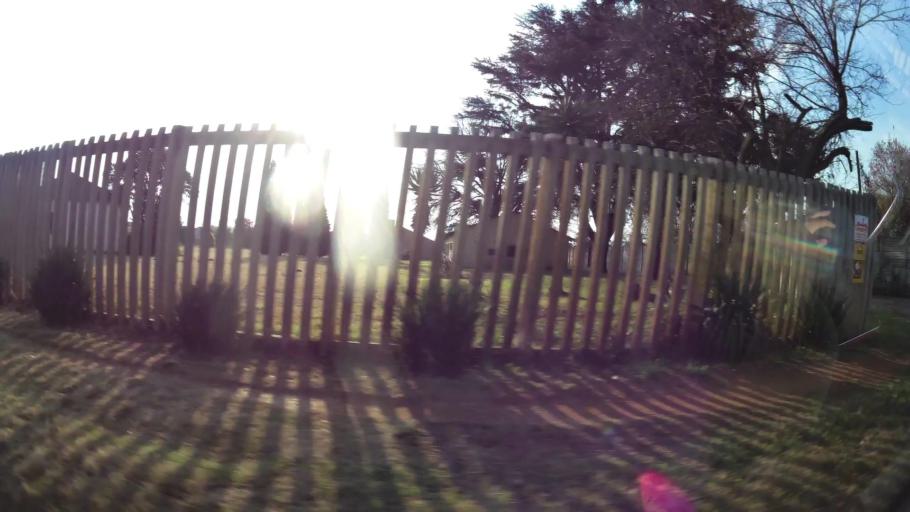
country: ZA
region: Gauteng
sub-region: Ekurhuleni Metropolitan Municipality
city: Benoni
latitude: -26.1111
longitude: 28.2933
